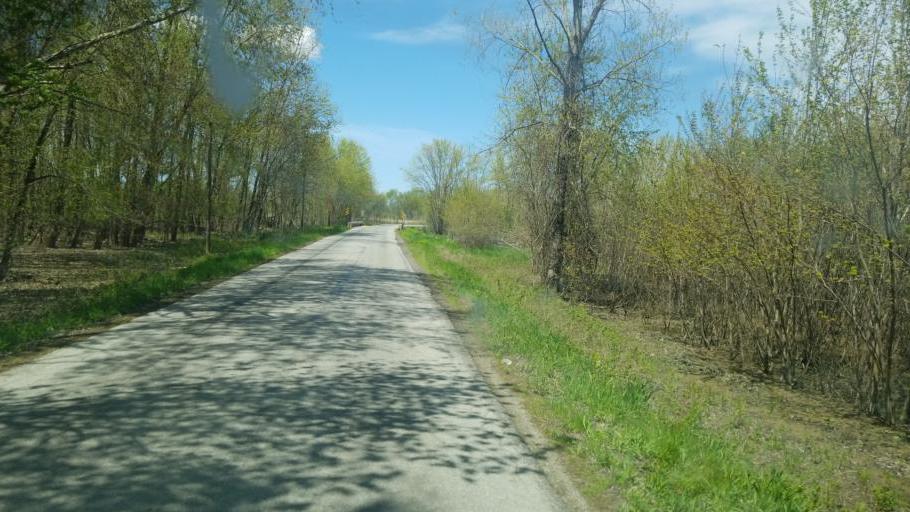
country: US
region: Ohio
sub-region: Wayne County
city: Shreve
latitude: 40.7571
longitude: -82.1176
